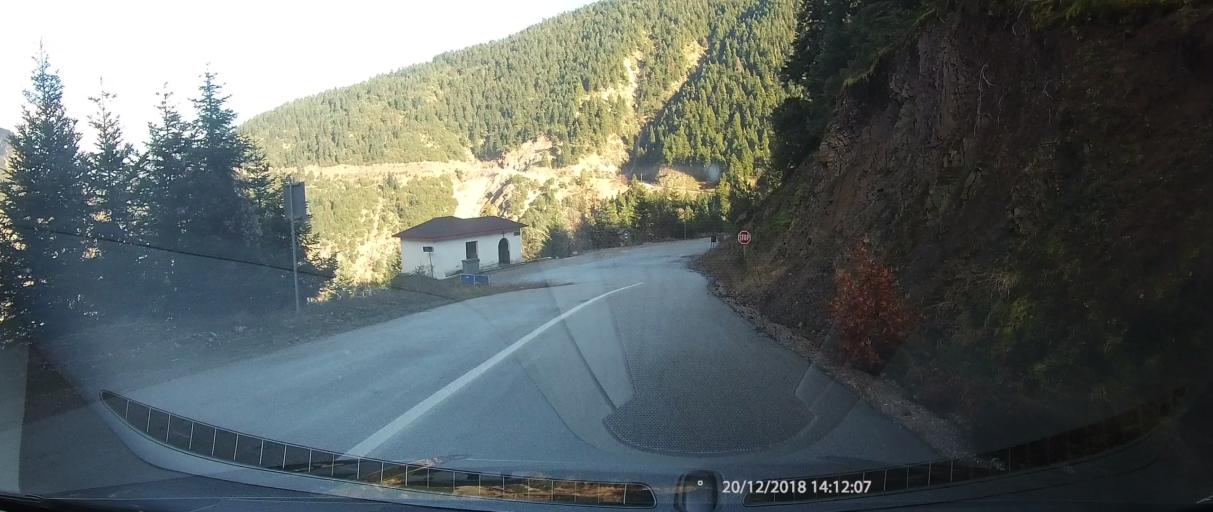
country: GR
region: West Greece
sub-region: Nomos Aitolias kai Akarnanias
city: Thermo
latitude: 38.7380
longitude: 21.6535
